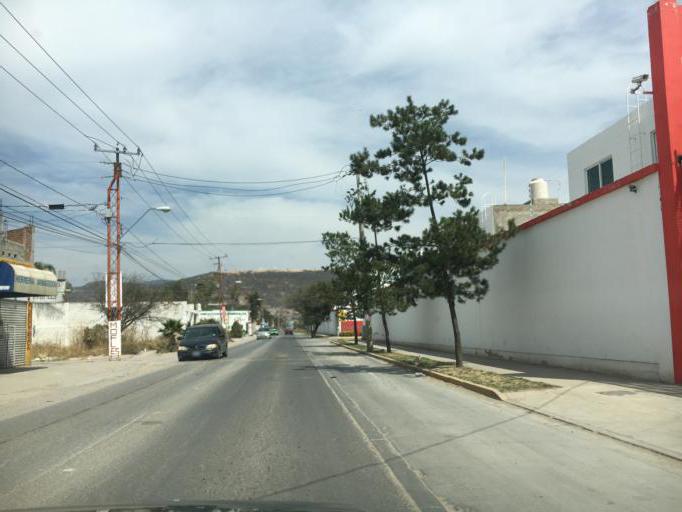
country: MX
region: Guanajuato
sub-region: Leon
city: Fraccionamiento Paraiso Real
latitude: 21.1104
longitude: -101.5932
